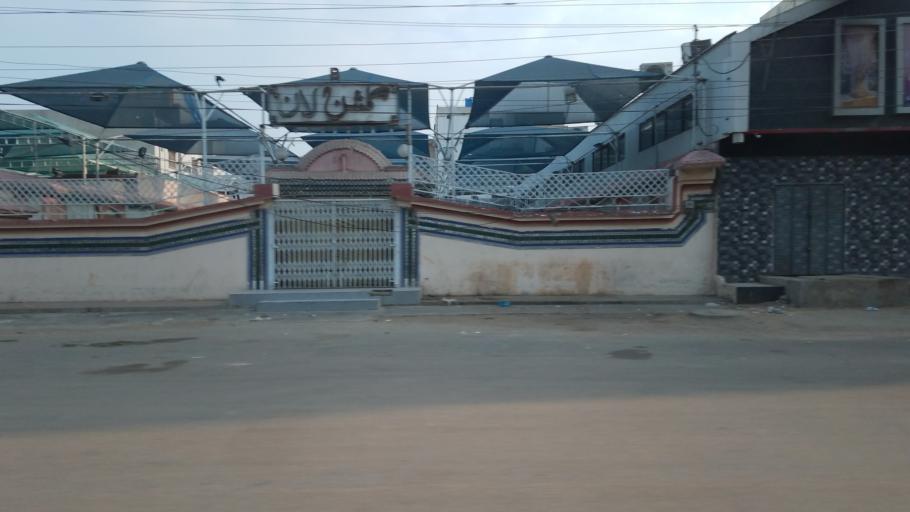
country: PK
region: Sindh
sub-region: Karachi District
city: Karachi
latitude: 24.9269
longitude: 67.0897
